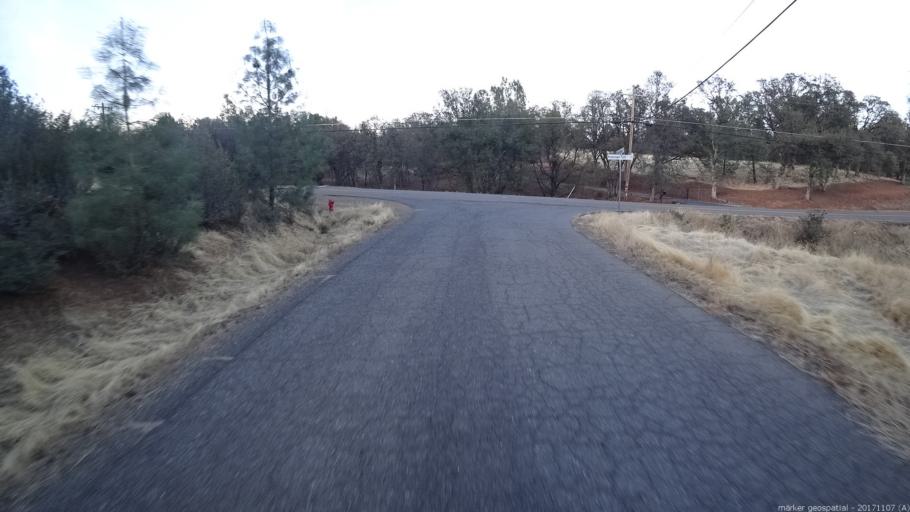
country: US
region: California
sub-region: Shasta County
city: Shasta
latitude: 40.5414
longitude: -122.4824
